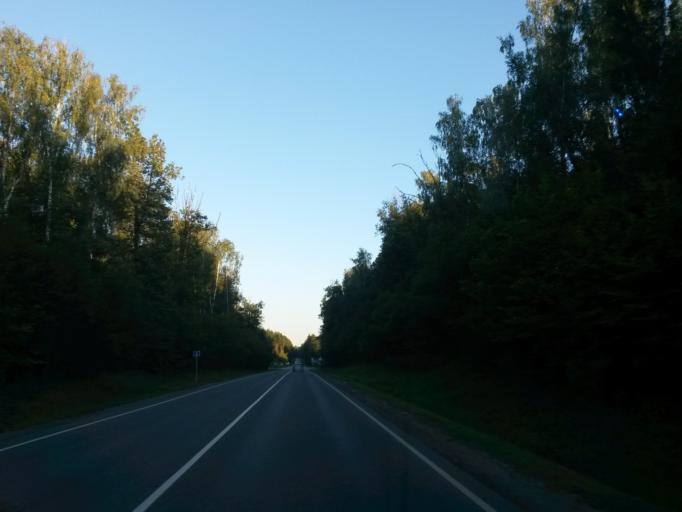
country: RU
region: Moskovskaya
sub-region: Podol'skiy Rayon
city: Podol'sk
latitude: 55.3841
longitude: 37.6278
